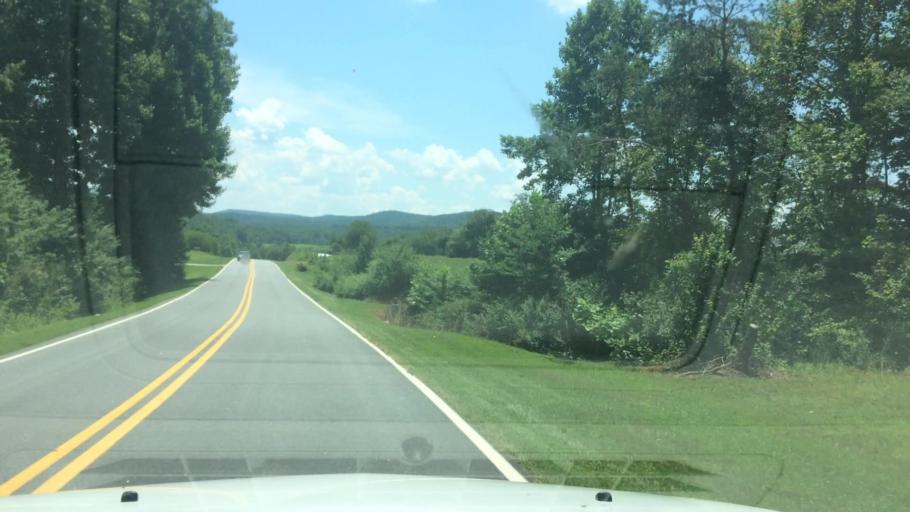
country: US
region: North Carolina
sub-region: Alexander County
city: Taylorsville
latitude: 35.9394
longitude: -81.2687
